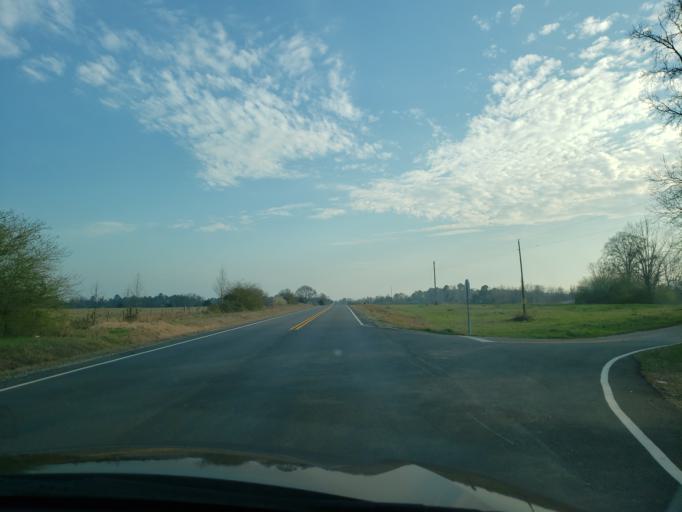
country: US
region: Alabama
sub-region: Hale County
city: Moundville
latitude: 32.8777
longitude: -87.6097
